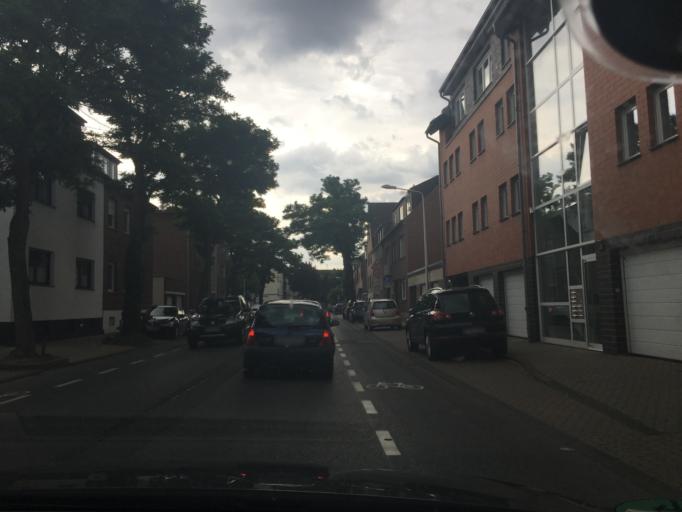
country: DE
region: North Rhine-Westphalia
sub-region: Regierungsbezirk Koln
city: Dueren
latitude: 50.7987
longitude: 6.4877
